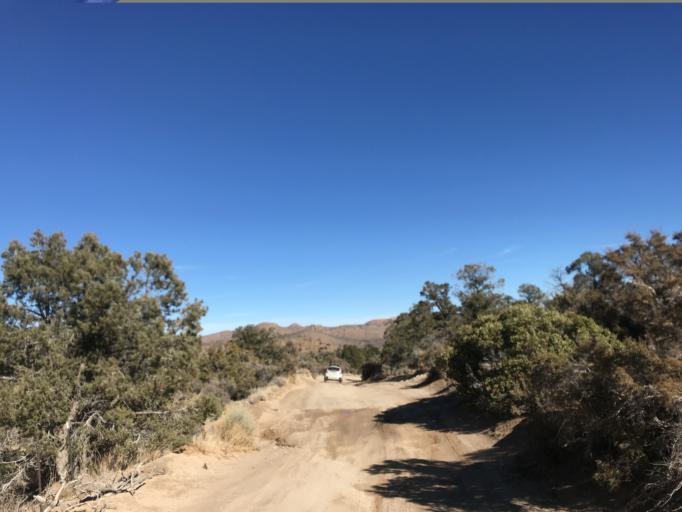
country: US
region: California
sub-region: San Bernardino County
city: Big Bear City
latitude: 34.2325
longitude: -116.6543
